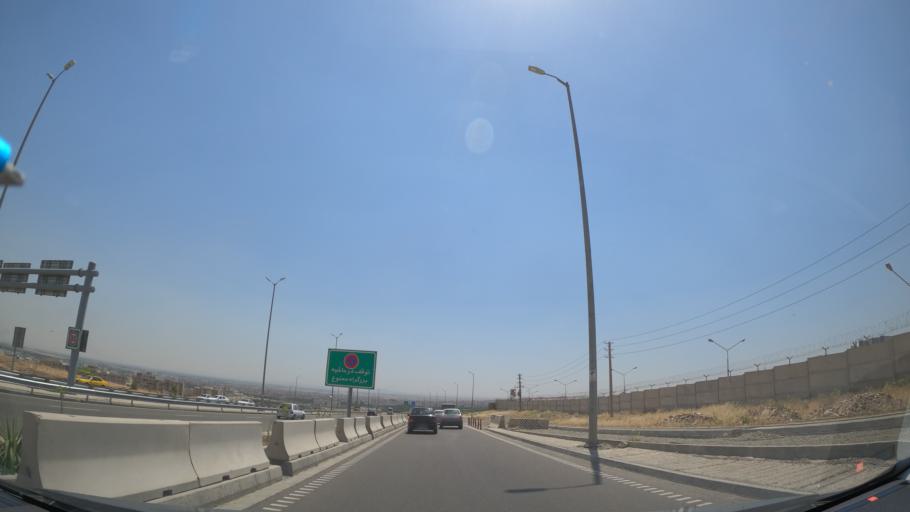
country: IR
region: Tehran
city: Shahr-e Qods
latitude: 35.7471
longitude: 51.1289
